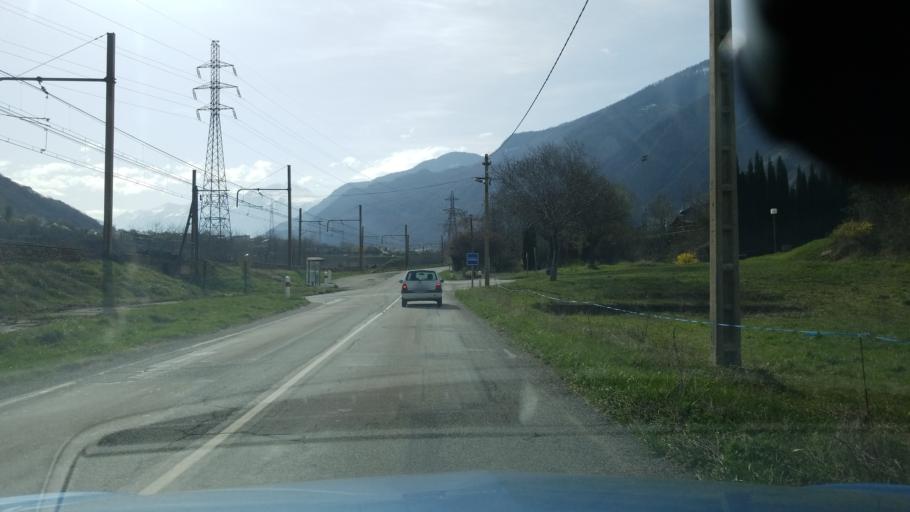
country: FR
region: Rhone-Alpes
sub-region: Departement de la Savoie
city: Villargondran
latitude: 45.2646
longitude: 6.3815
